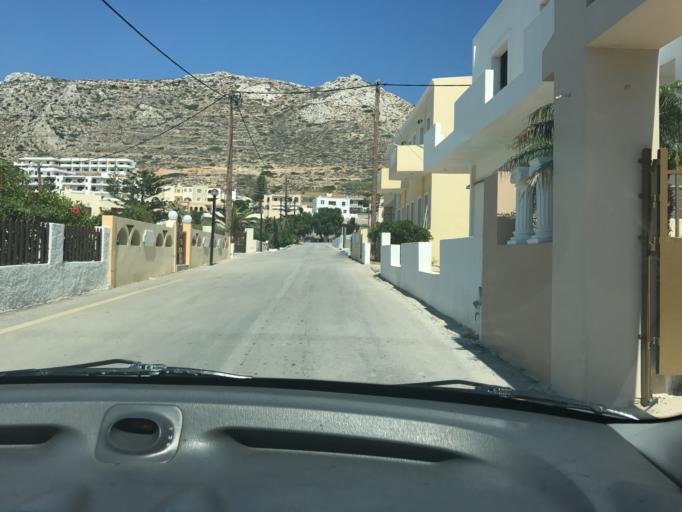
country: GR
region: South Aegean
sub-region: Nomos Dodekanisou
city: Karpathos
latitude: 35.4791
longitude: 27.1186
